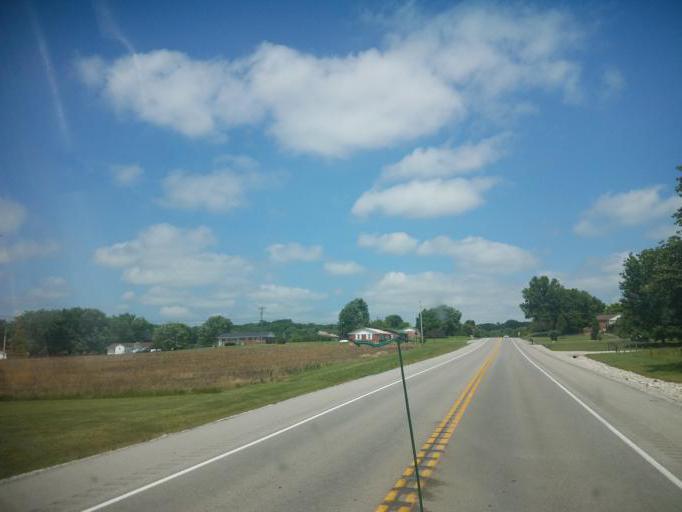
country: US
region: Kentucky
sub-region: Barren County
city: Glasgow
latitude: 36.9414
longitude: -85.8311
